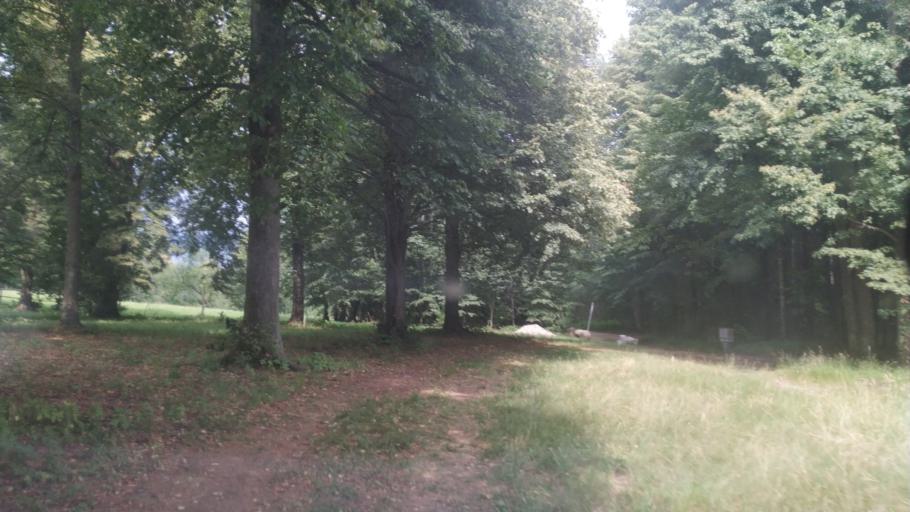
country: IT
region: Piedmont
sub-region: Provincia di Vercelli
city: Varallo
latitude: 45.7985
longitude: 8.2447
